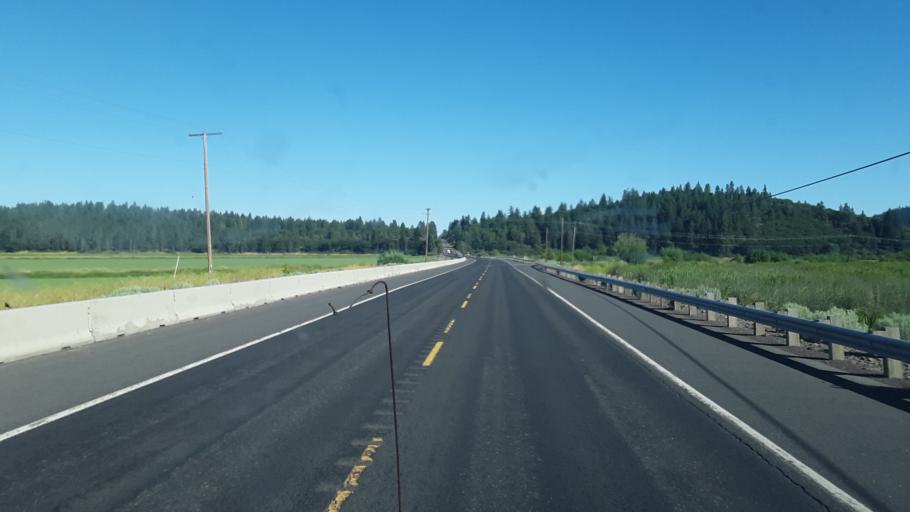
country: US
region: Oregon
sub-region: Klamath County
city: Klamath Falls
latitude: 42.2892
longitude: -121.9253
